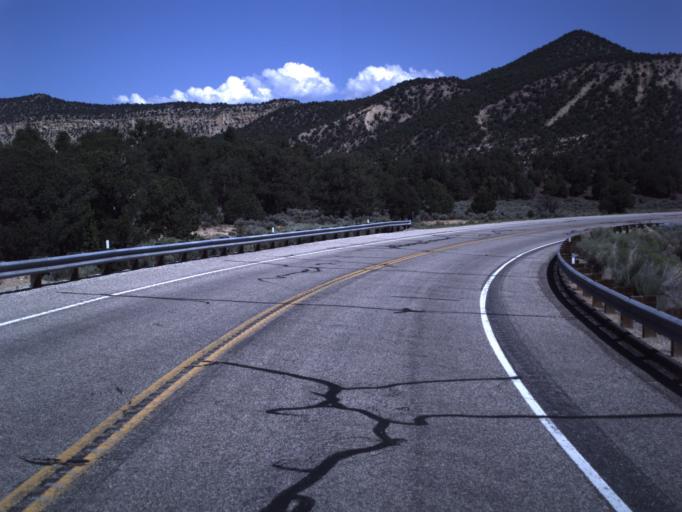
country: US
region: Utah
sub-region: Wayne County
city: Loa
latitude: 38.7264
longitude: -111.4011
